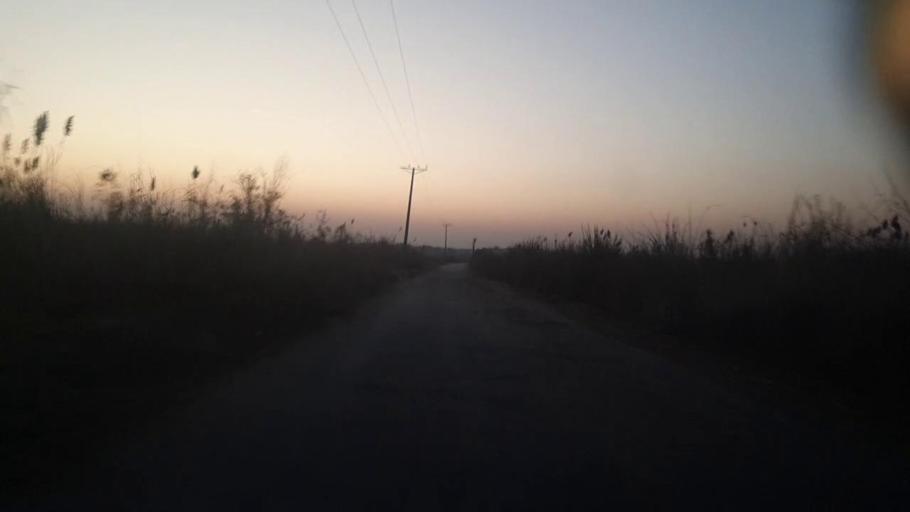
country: PK
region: Sindh
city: Kandiari
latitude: 26.6865
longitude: 68.9138
